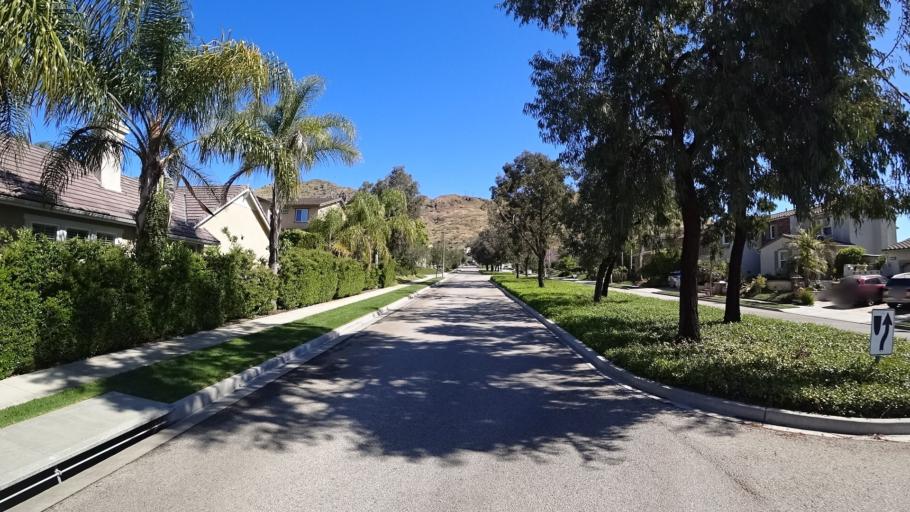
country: US
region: California
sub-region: Ventura County
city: Casa Conejo
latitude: 34.1779
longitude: -118.9836
